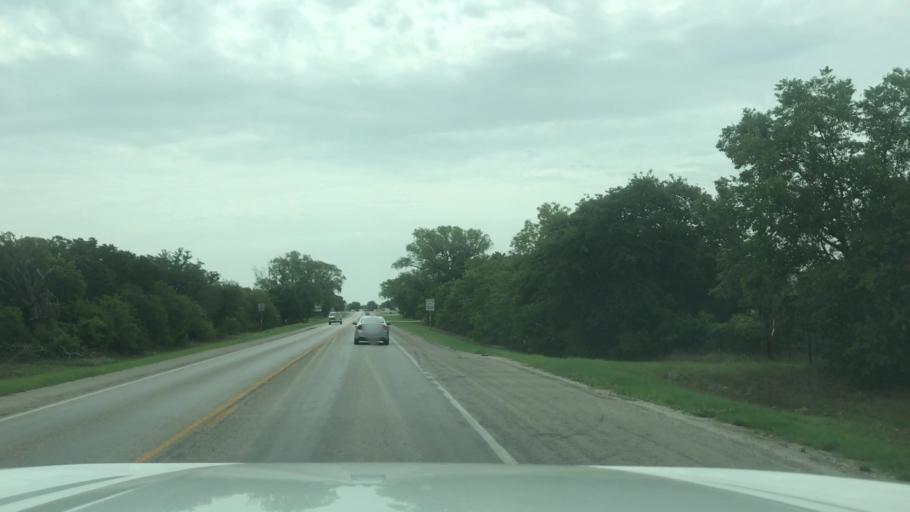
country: US
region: Texas
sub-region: Eastland County
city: Gorman
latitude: 32.2192
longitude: -98.6774
